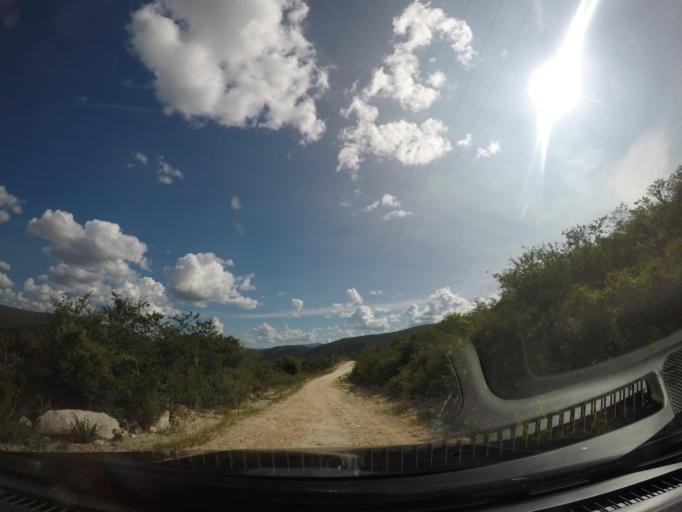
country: BR
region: Bahia
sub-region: Barra Da Estiva
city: Barra da Estiva
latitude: -13.2144
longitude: -41.5937
